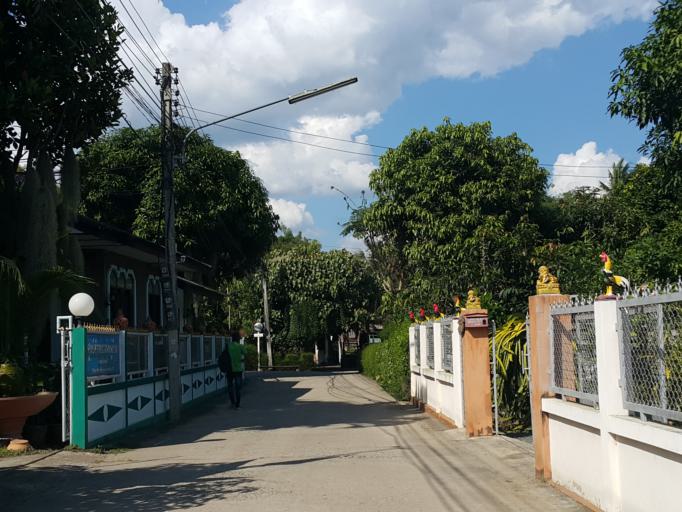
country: TH
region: Chiang Mai
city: San Sai
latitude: 18.9309
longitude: 98.9195
